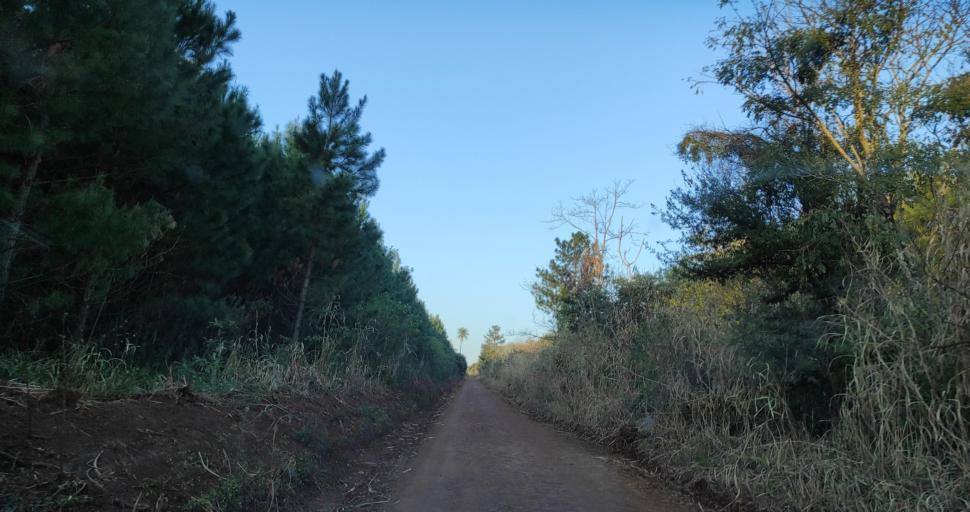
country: AR
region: Misiones
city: Capiovi
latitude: -26.8807
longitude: -55.1111
